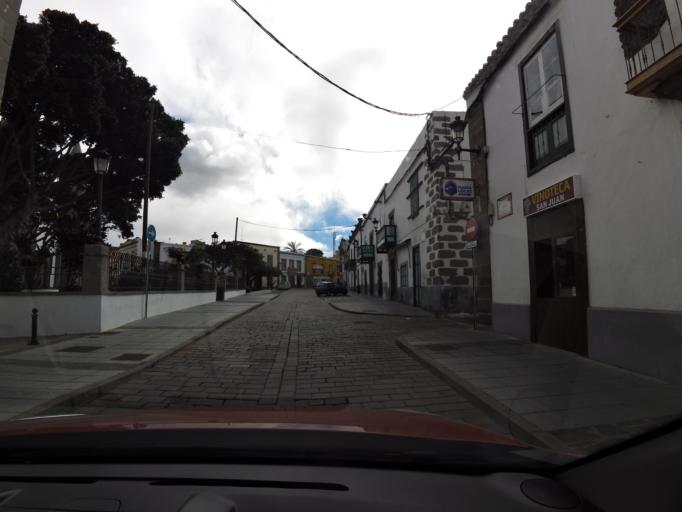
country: ES
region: Canary Islands
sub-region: Provincia de Las Palmas
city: Telde
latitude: 28.0037
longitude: -15.4145
